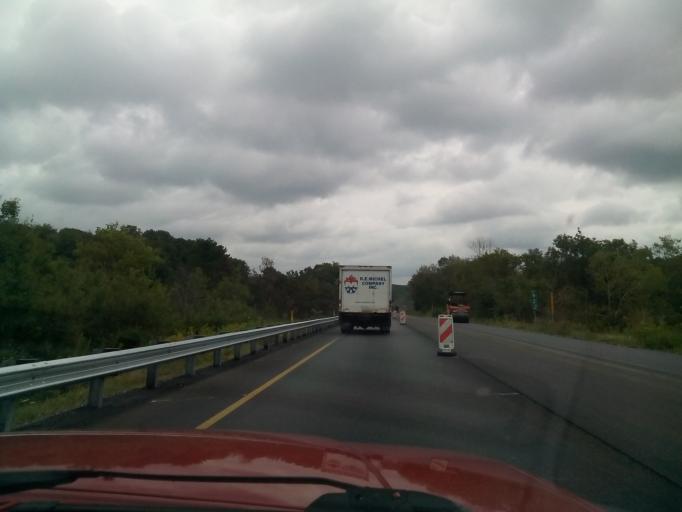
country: US
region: Pennsylvania
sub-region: Jefferson County
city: Reynoldsville
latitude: 41.1504
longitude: -78.8661
